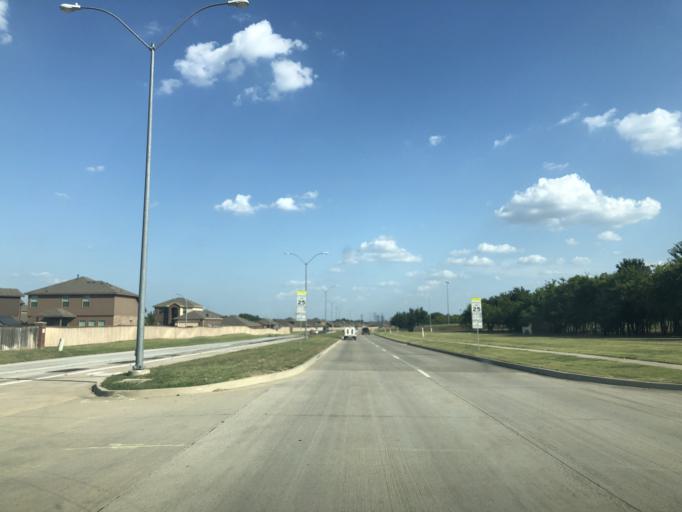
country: US
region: Texas
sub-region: Tarrant County
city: Saginaw
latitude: 32.8401
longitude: -97.3867
